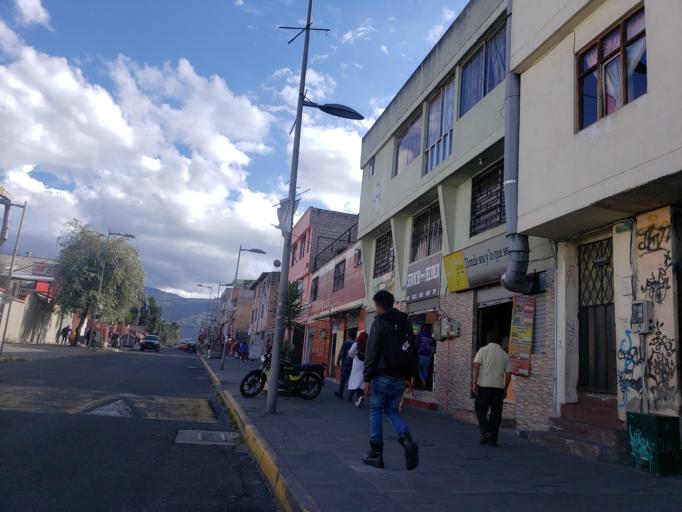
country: EC
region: Pichincha
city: Quito
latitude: -0.2672
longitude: -78.5385
